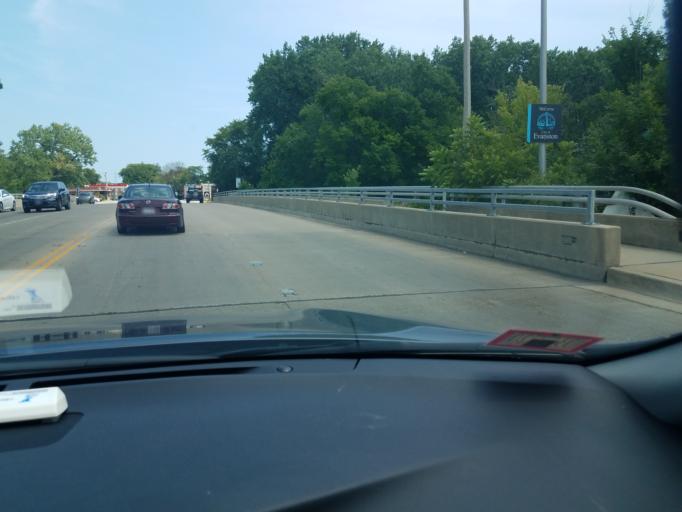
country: US
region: Illinois
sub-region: Cook County
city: Evanston
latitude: 42.0409
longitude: -87.7102
